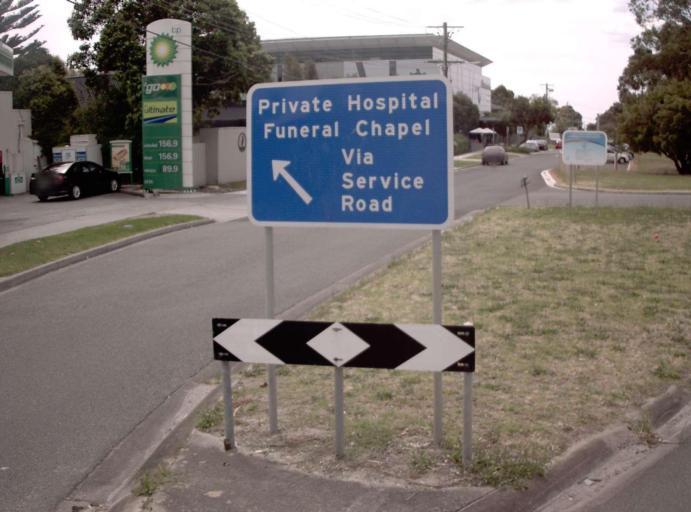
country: AU
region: Victoria
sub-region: Frankston
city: Frankston South
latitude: -38.1551
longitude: 145.1340
